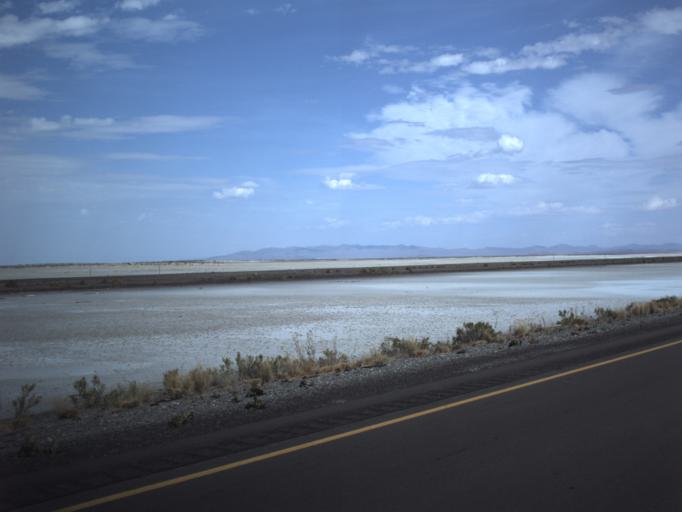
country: US
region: Utah
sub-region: Tooele County
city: Wendover
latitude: 40.7298
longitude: -113.4530
